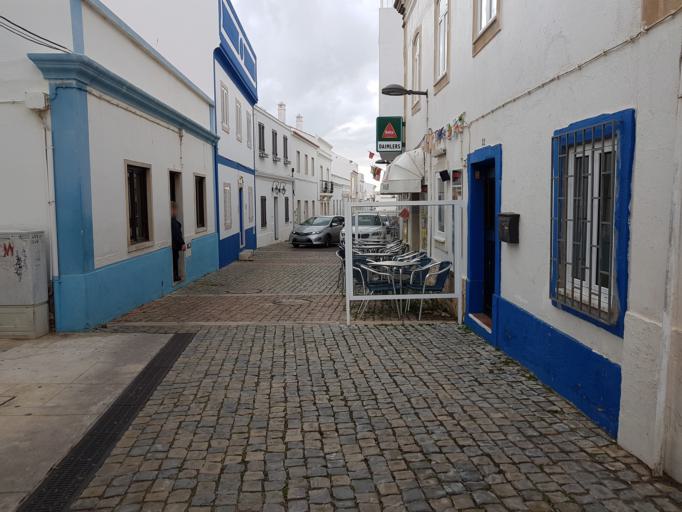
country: PT
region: Faro
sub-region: Albufeira
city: Albufeira
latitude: 37.0853
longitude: -8.2561
